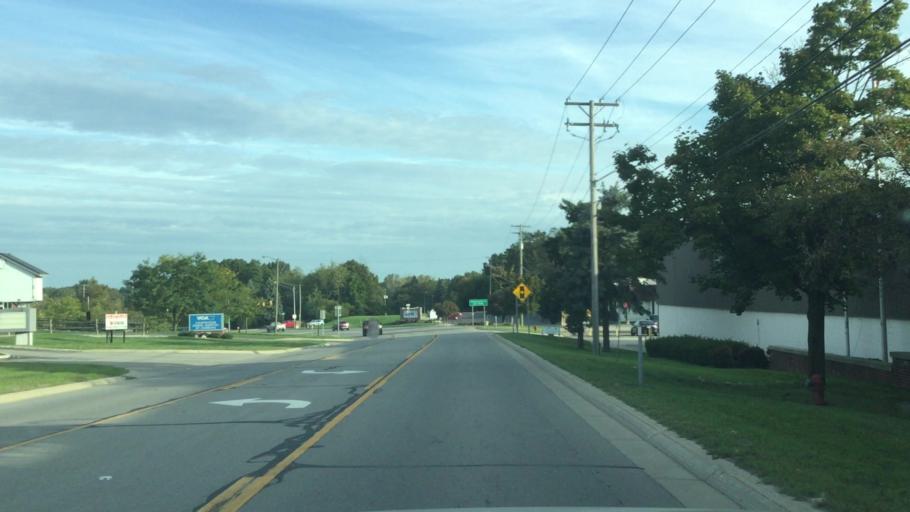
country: US
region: Michigan
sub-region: Livingston County
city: Whitmore Lake
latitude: 42.4547
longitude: -83.7986
